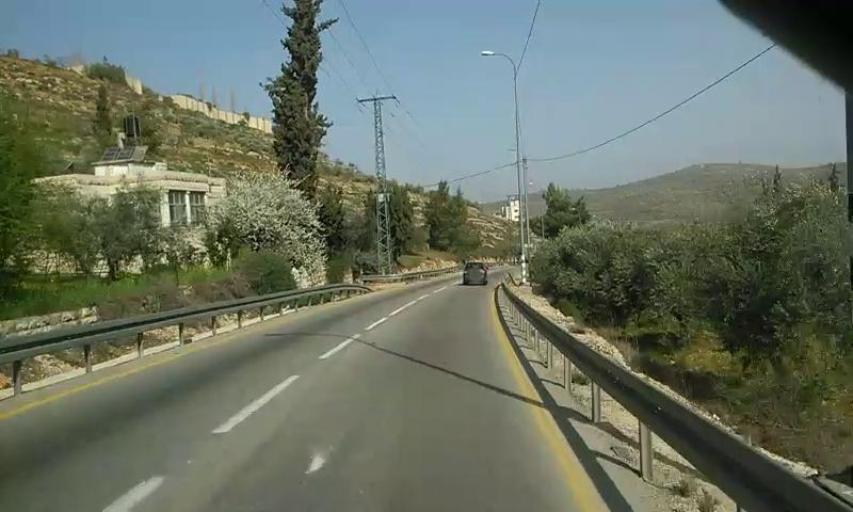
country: PS
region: West Bank
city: Sinjil
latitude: 32.0354
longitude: 35.2717
